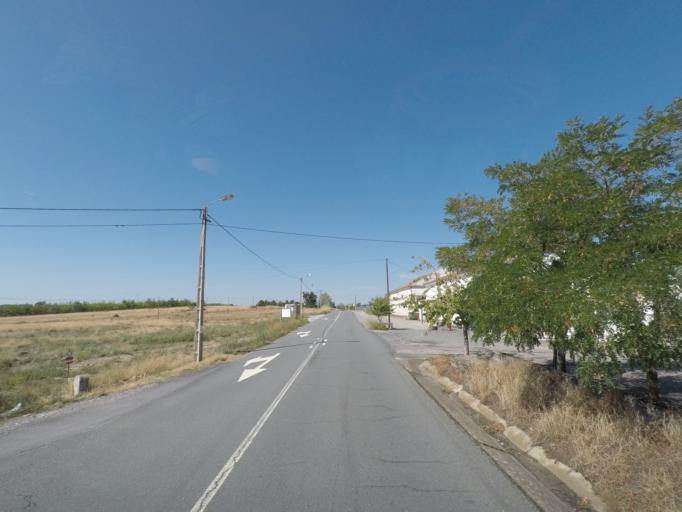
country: ES
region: Castille and Leon
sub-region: Provincia de Salamanca
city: Villarino de los Aires
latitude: 41.3670
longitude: -6.4966
